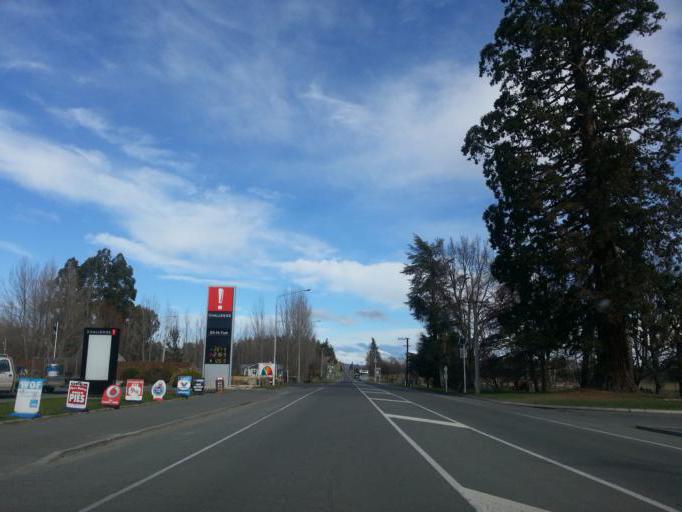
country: NZ
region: Canterbury
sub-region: Hurunui District
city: Amberley
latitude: -42.7753
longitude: 172.8471
